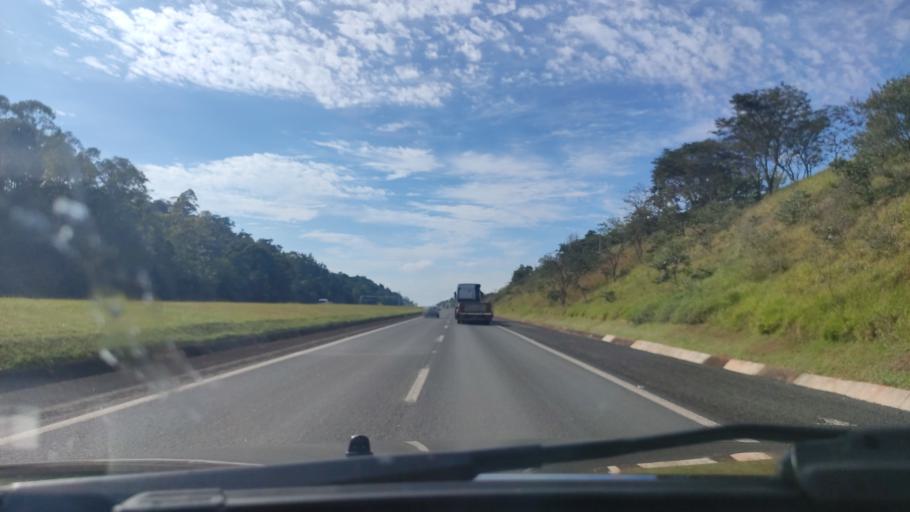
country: BR
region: Sao Paulo
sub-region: Itatinga
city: Itatinga
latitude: -23.0607
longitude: -48.5714
